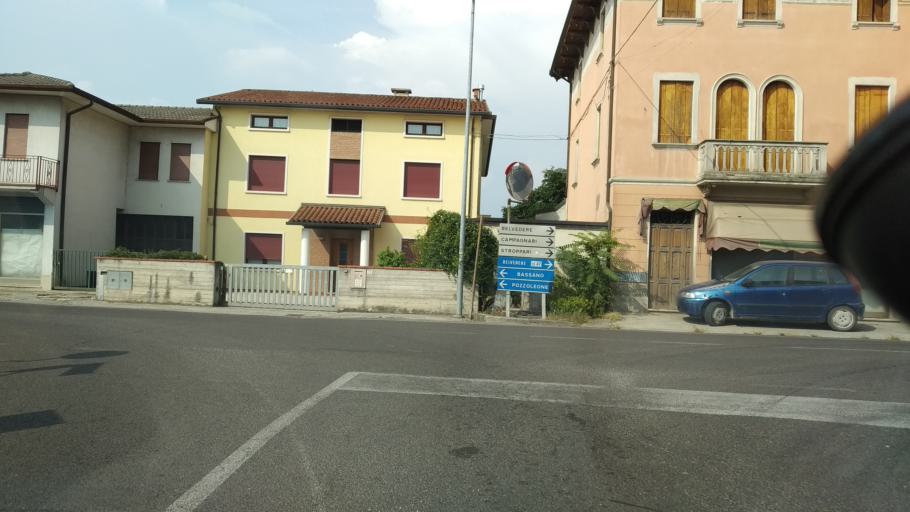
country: IT
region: Veneto
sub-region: Provincia di Vicenza
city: Tezze
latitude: 45.6820
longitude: 11.7067
